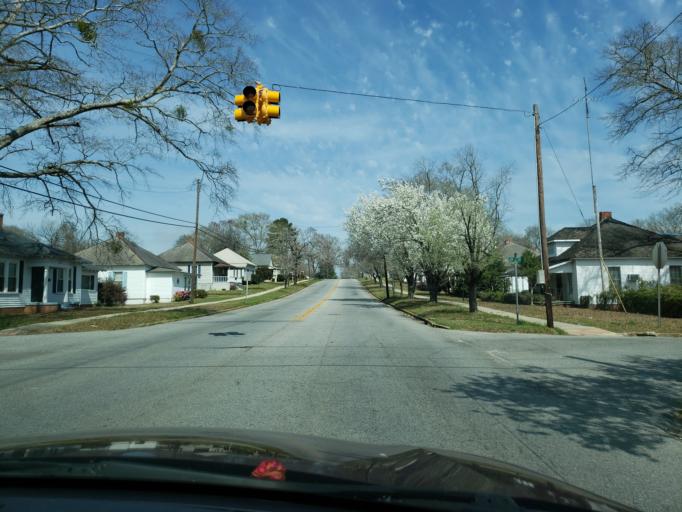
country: US
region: Alabama
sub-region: Elmore County
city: Tallassee
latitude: 32.5352
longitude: -85.8816
